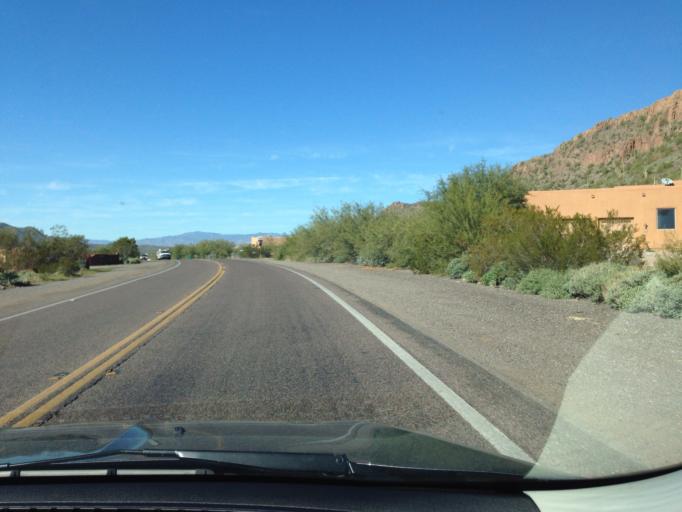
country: US
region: Arizona
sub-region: Maricopa County
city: Anthem
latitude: 33.8654
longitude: -112.0589
